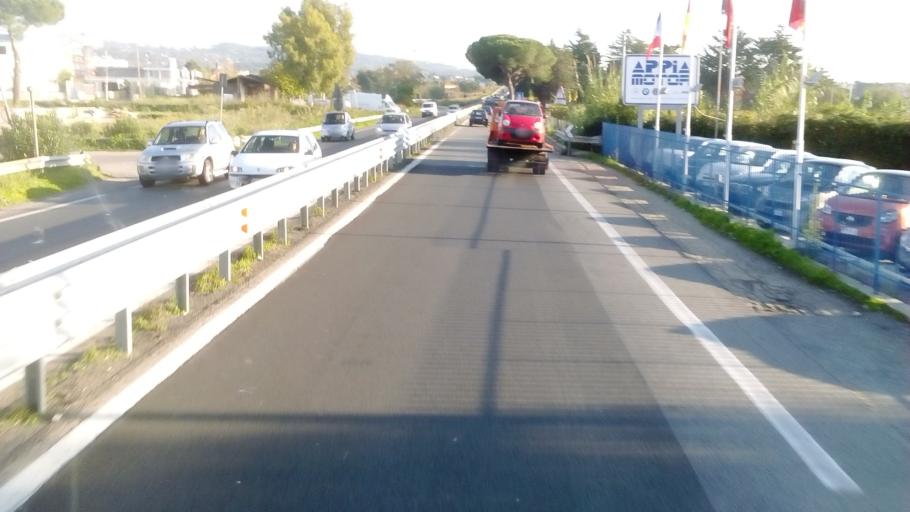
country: IT
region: Latium
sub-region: Citta metropolitana di Roma Capitale
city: Ciampino
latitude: 41.7816
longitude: 12.6025
